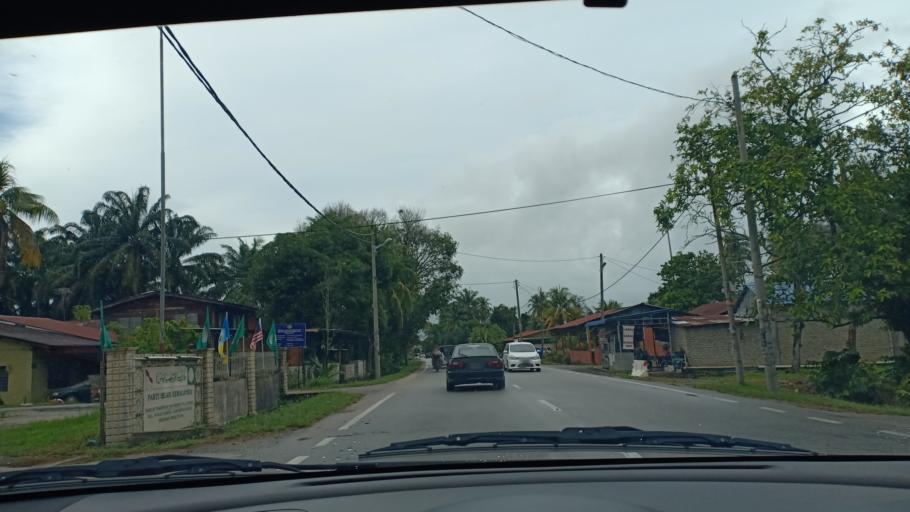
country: MY
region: Penang
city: Kepala Batas
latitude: 5.4974
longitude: 100.4412
